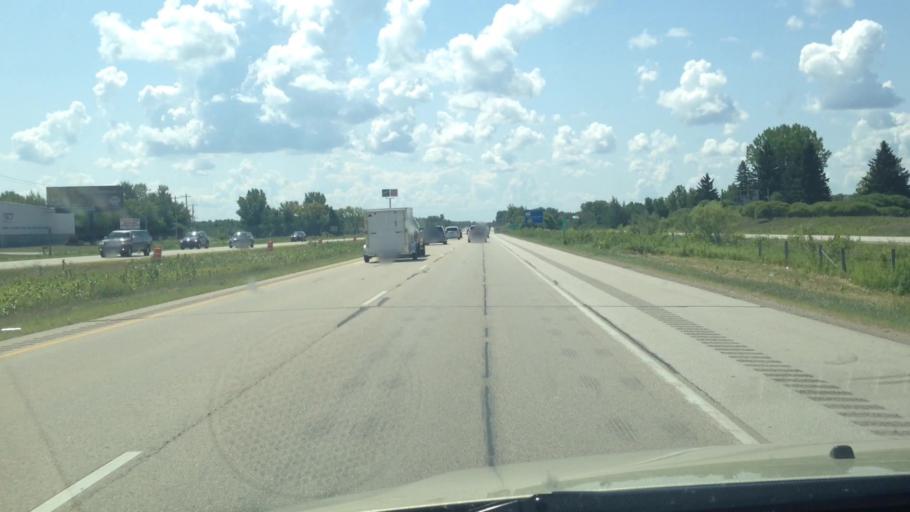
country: US
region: Wisconsin
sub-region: Brown County
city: Suamico
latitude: 44.6869
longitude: -88.0506
